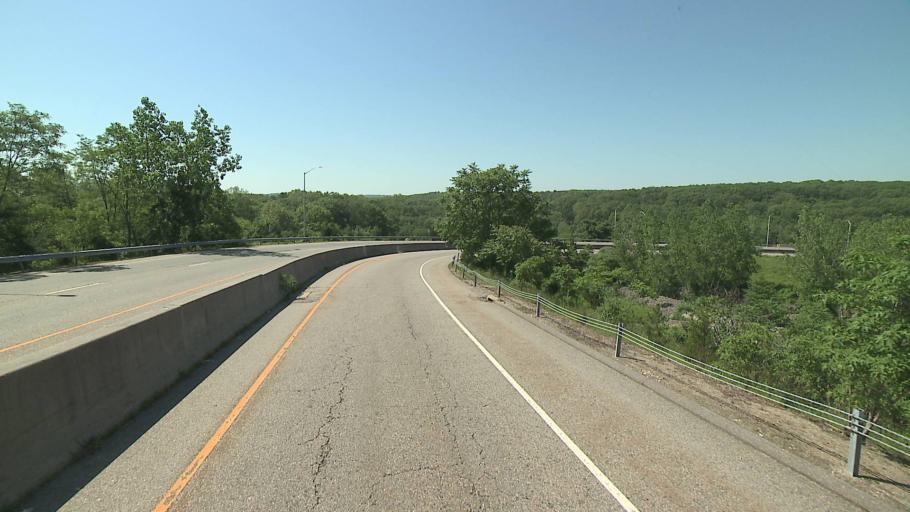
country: US
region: Connecticut
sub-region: New London County
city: Norwich
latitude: 41.4809
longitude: -72.0785
